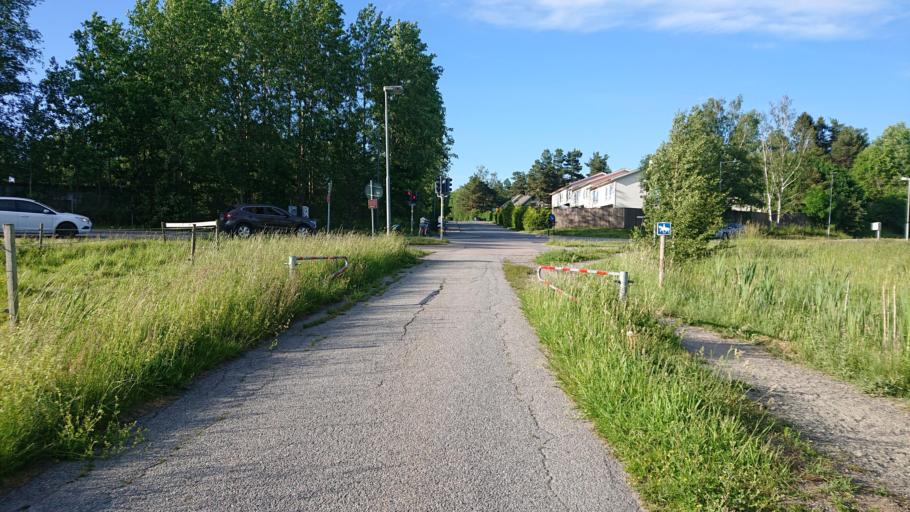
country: SE
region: Stockholm
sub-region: Osterakers Kommun
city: Akersberga
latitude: 59.5036
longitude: 18.2957
